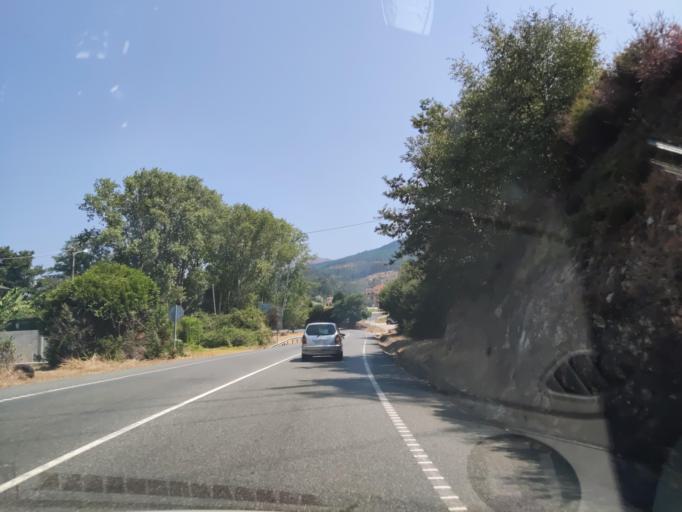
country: ES
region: Galicia
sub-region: Provincia de Pontevedra
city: Porrino
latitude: 42.1934
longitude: -8.6073
